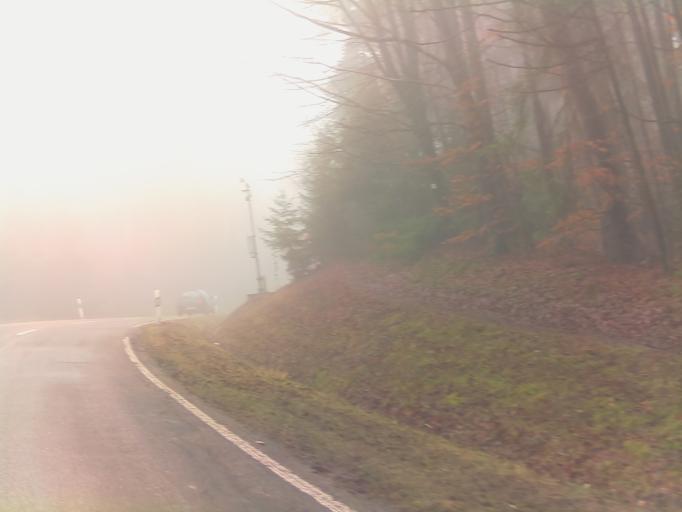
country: DE
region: Bavaria
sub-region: Regierungsbezirk Unterfranken
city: Altenbuch
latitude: 49.8320
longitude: 9.3641
